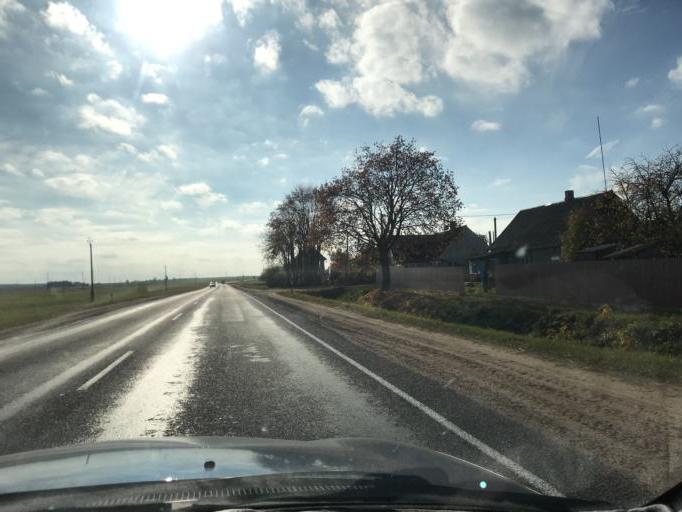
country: BY
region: Grodnenskaya
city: Voranava
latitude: 54.1539
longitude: 25.3259
